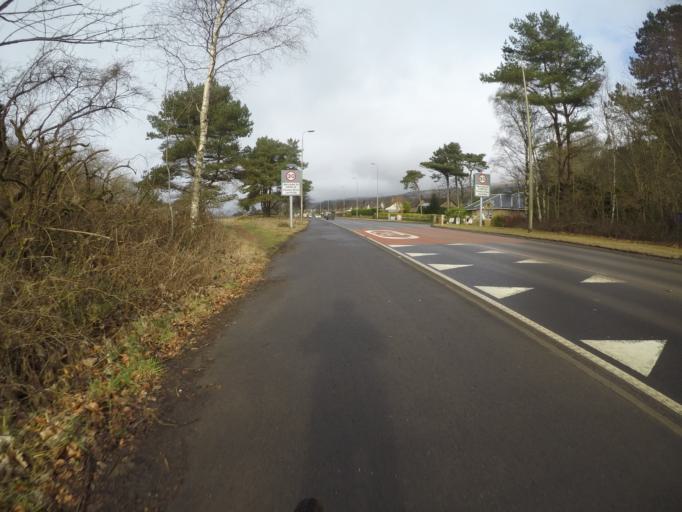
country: GB
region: Scotland
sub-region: North Ayrshire
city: Fairlie
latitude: 55.7463
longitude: -4.8573
